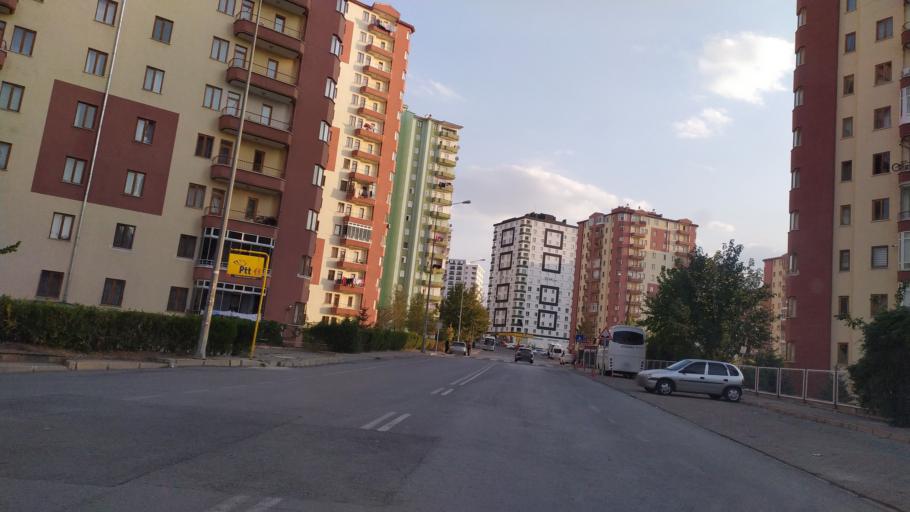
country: TR
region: Kayseri
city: Talas
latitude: 38.7053
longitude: 35.5614
